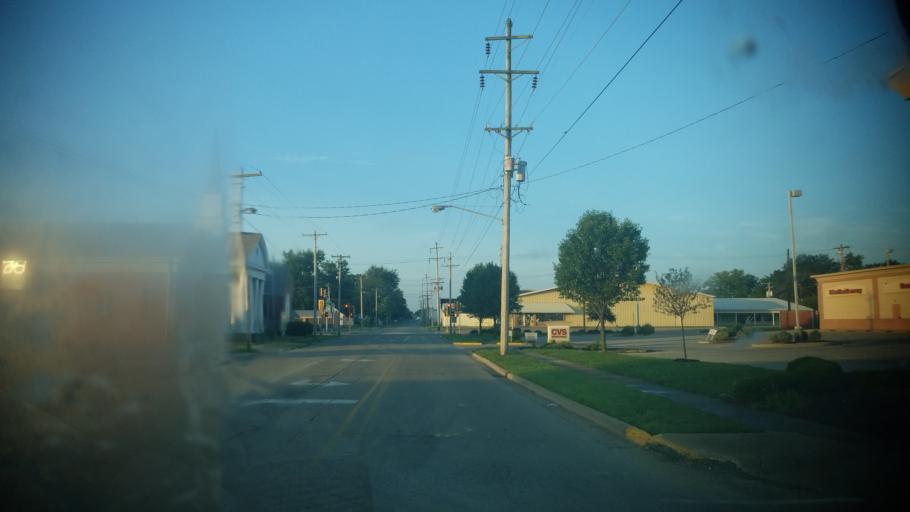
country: US
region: Illinois
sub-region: Wayne County
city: Fairfield
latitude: 38.3797
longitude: -88.3685
